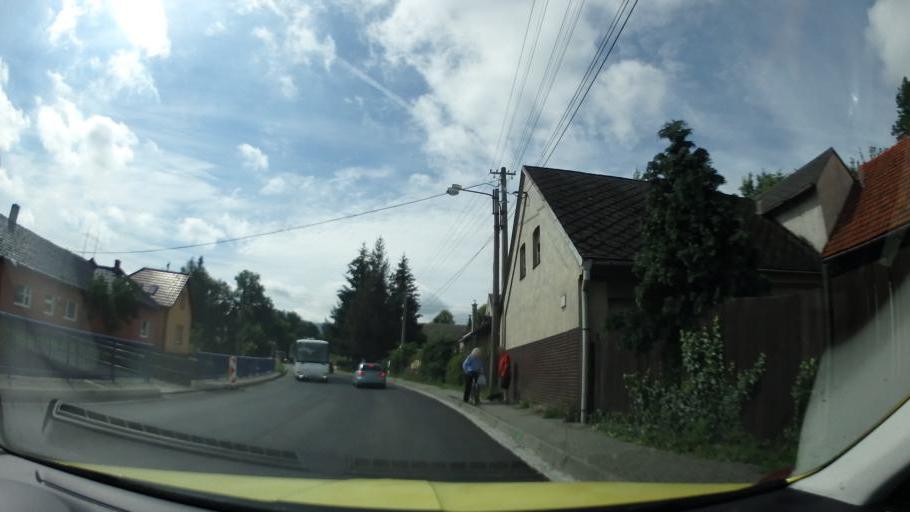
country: CZ
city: Hodslavice
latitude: 49.5453
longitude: 18.0247
